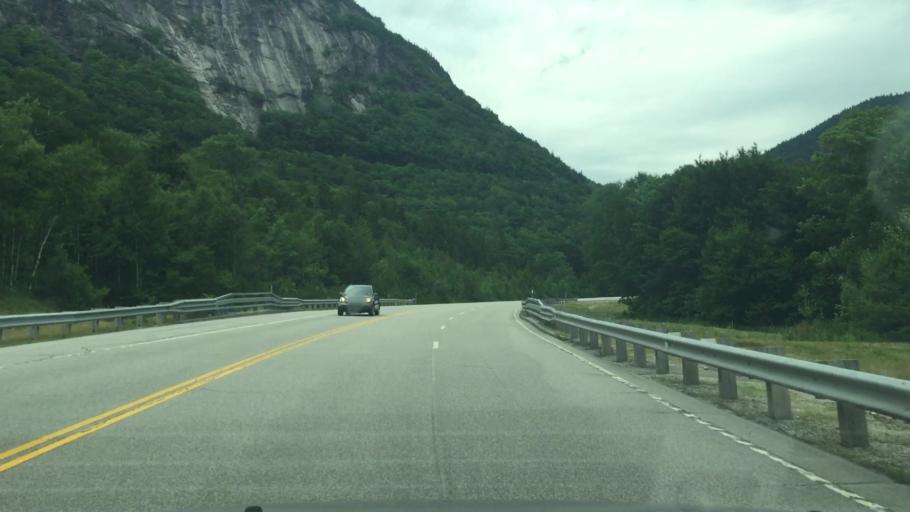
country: US
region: New Hampshire
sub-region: Grafton County
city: Deerfield
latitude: 44.1975
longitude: -71.4071
